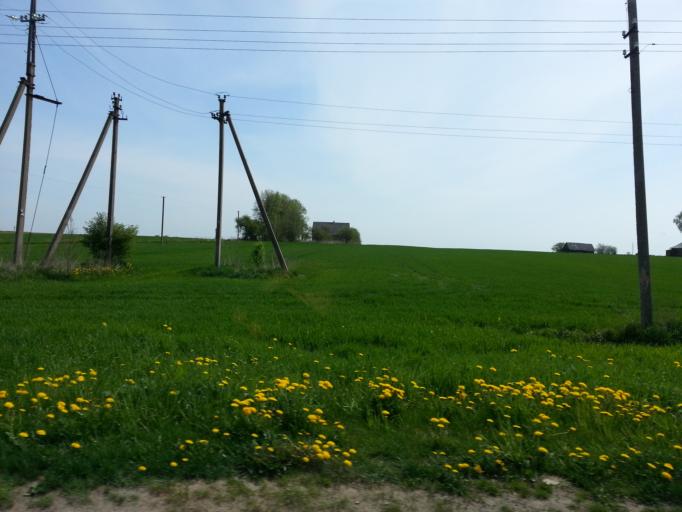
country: LT
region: Panevezys
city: Pasvalys
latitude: 55.9221
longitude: 24.2359
